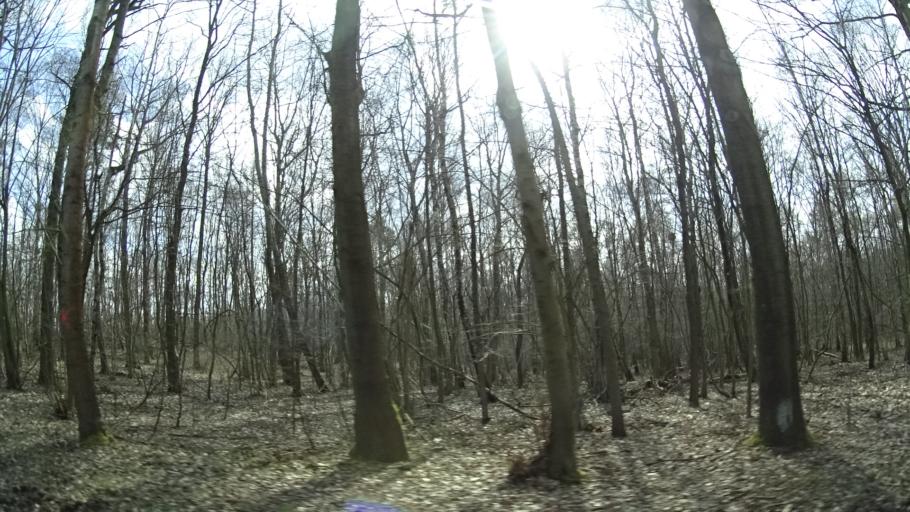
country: DE
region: Saxony-Anhalt
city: Schonburg
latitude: 51.1574
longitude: 11.8815
